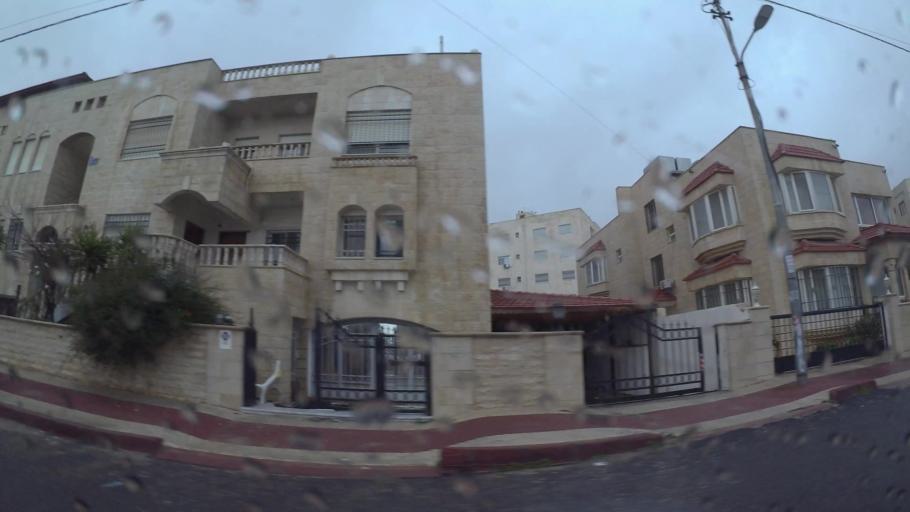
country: JO
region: Amman
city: Al Jubayhah
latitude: 32.0348
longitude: 35.8882
